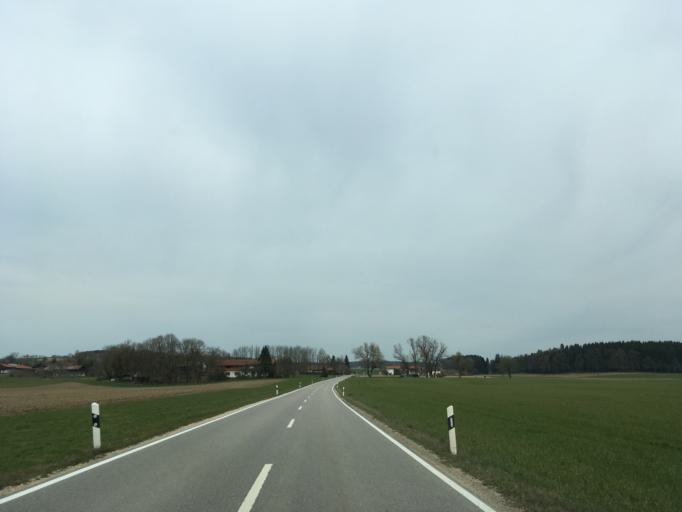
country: DE
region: Bavaria
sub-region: Upper Bavaria
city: Hoslwang
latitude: 47.9677
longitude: 12.3519
